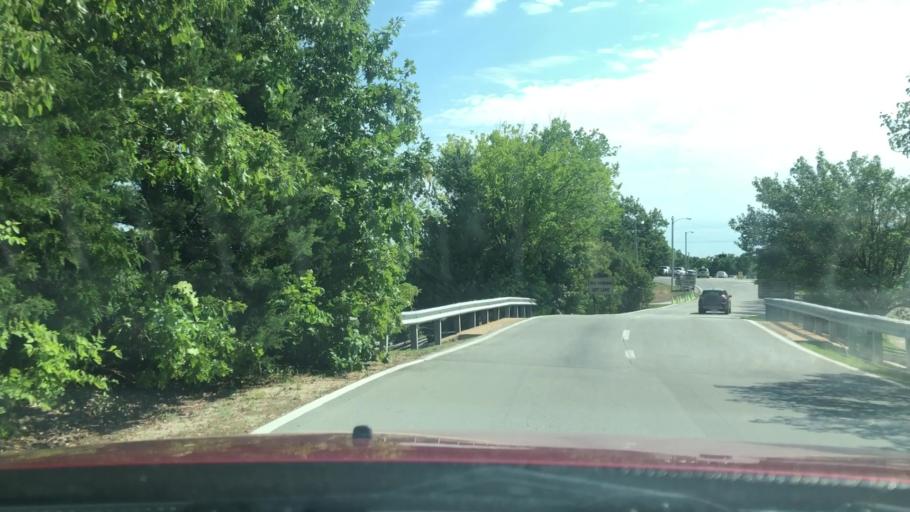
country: US
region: Missouri
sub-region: Stone County
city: Kimberling City
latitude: 36.6632
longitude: -93.3378
